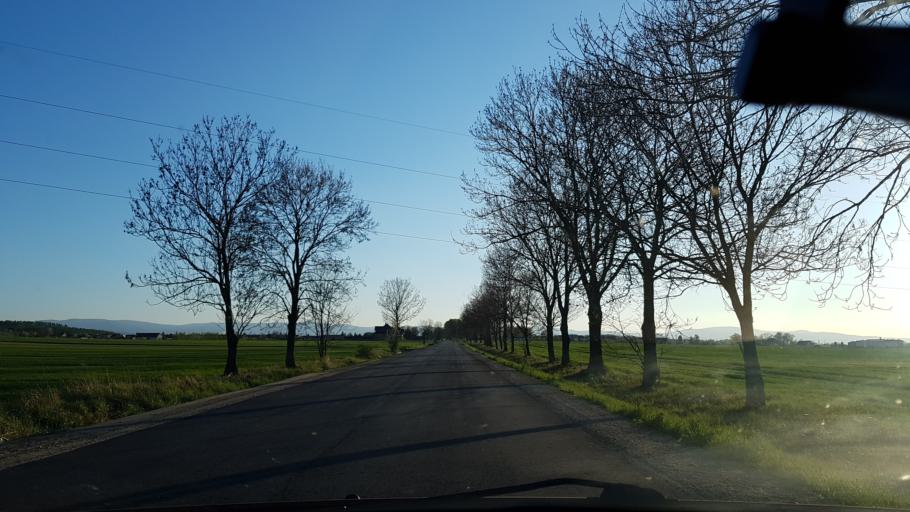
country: CZ
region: Olomoucky
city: Vidnava
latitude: 50.4250
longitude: 17.2364
